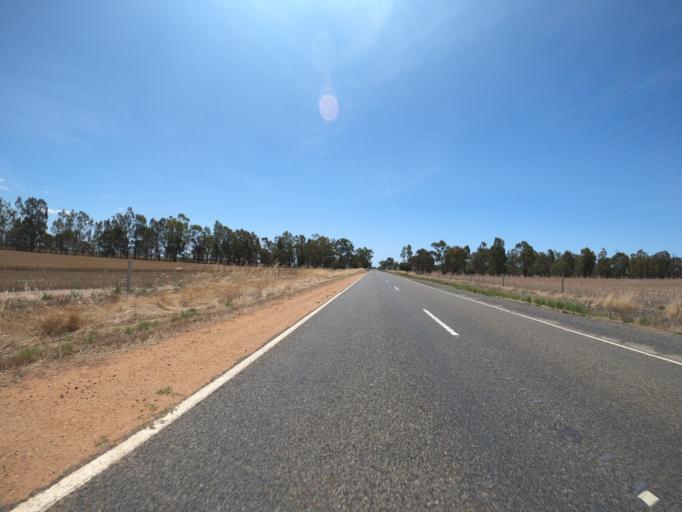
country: AU
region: Victoria
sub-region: Moira
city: Yarrawonga
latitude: -36.1617
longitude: 145.9672
